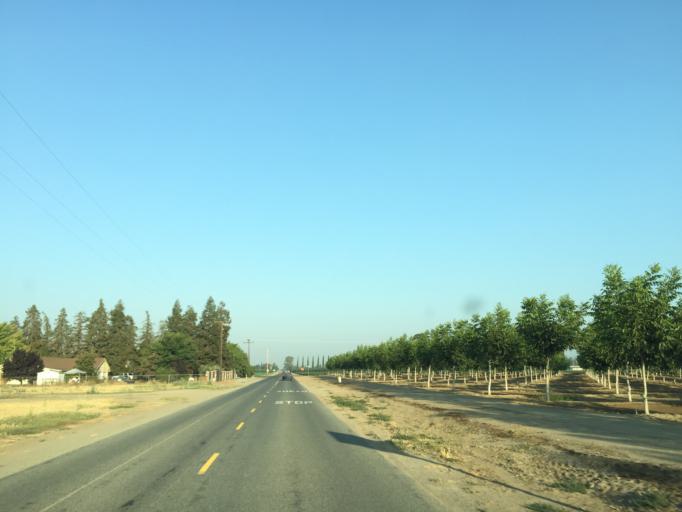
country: US
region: California
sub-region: Tulare County
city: Visalia
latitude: 36.3710
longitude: -119.2766
